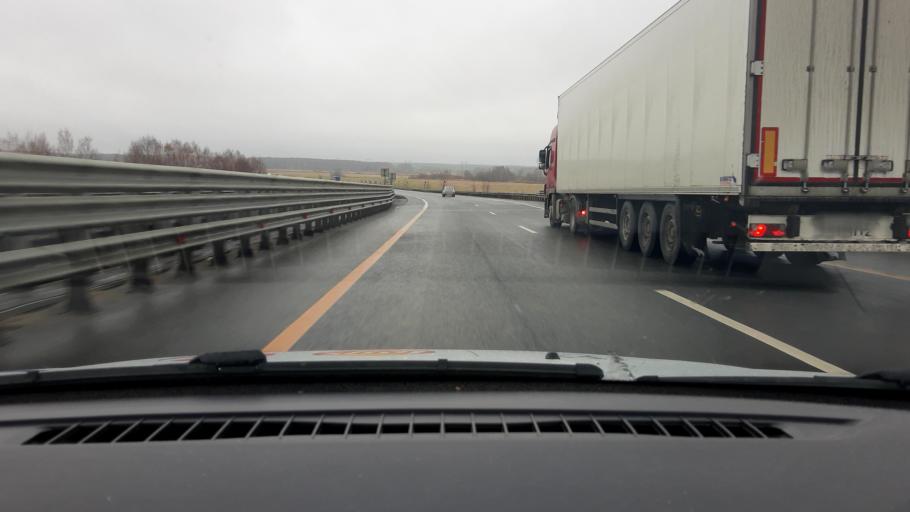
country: RU
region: Nizjnij Novgorod
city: Burevestnik
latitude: 56.1274
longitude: 43.7852
